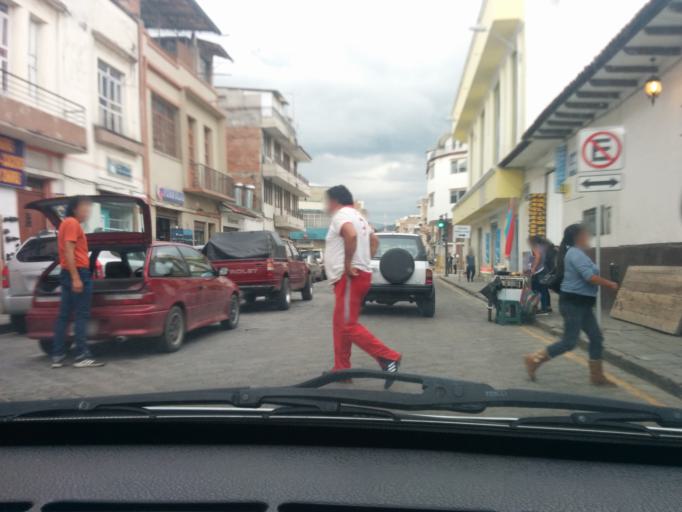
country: EC
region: Azuay
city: Cuenca
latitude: -2.8980
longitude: -78.9979
